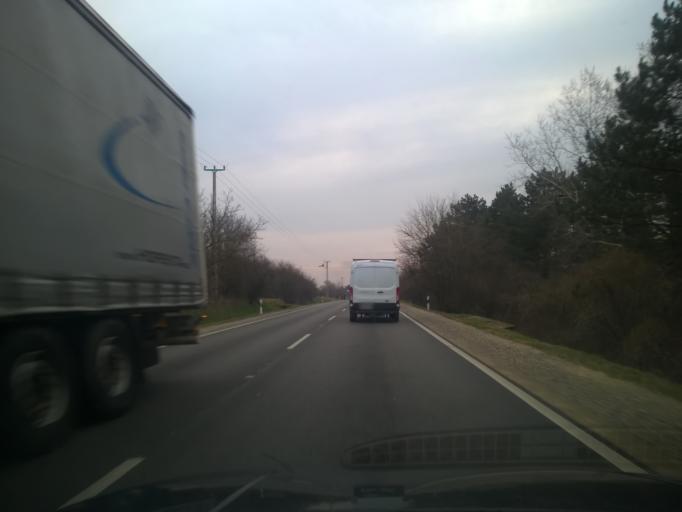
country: HU
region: Baranya
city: Pellerd
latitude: 46.0618
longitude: 18.1285
